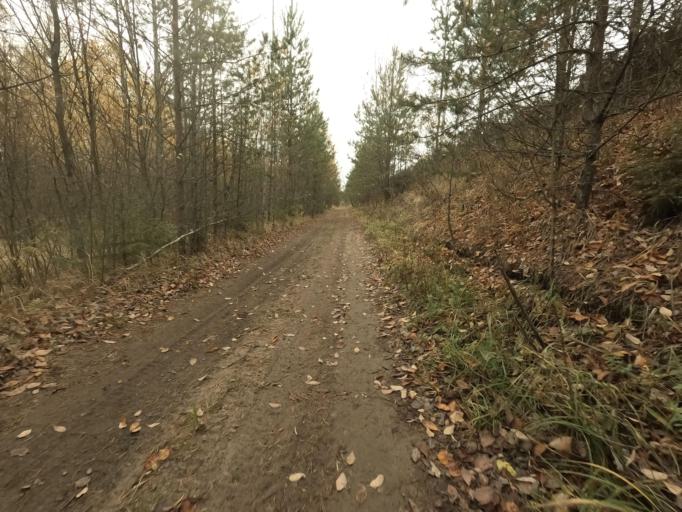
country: RU
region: Leningrad
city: Pavlovo
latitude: 59.7733
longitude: 30.9037
